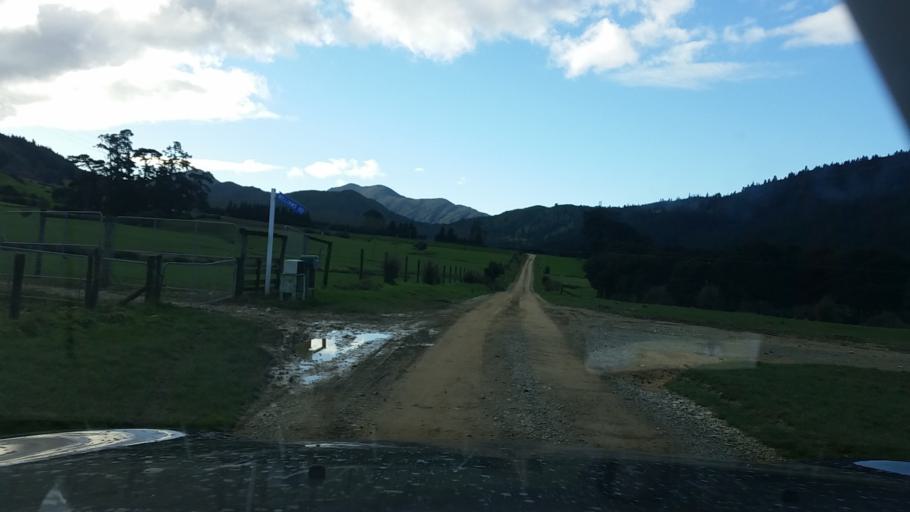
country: NZ
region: Marlborough
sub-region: Marlborough District
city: Picton
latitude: -41.1558
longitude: 174.1294
